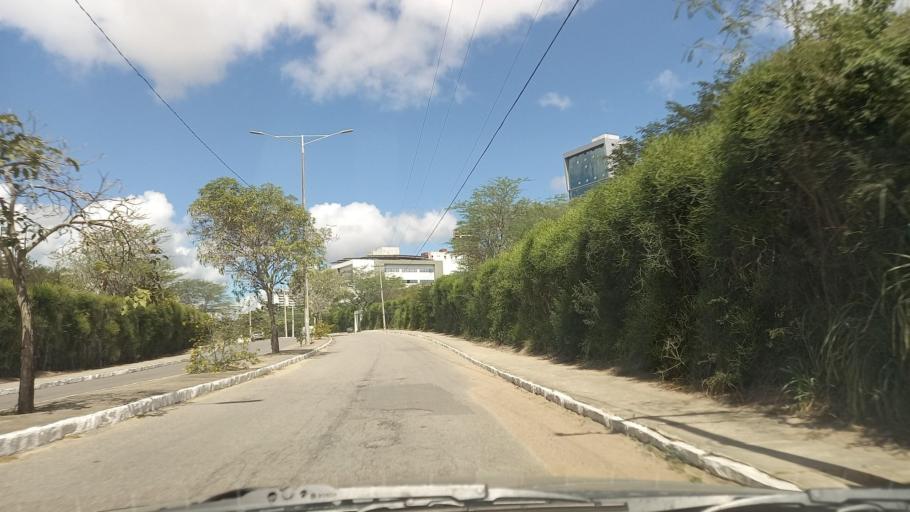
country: BR
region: Pernambuco
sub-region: Caruaru
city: Caruaru
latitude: -8.2590
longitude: -35.9642
